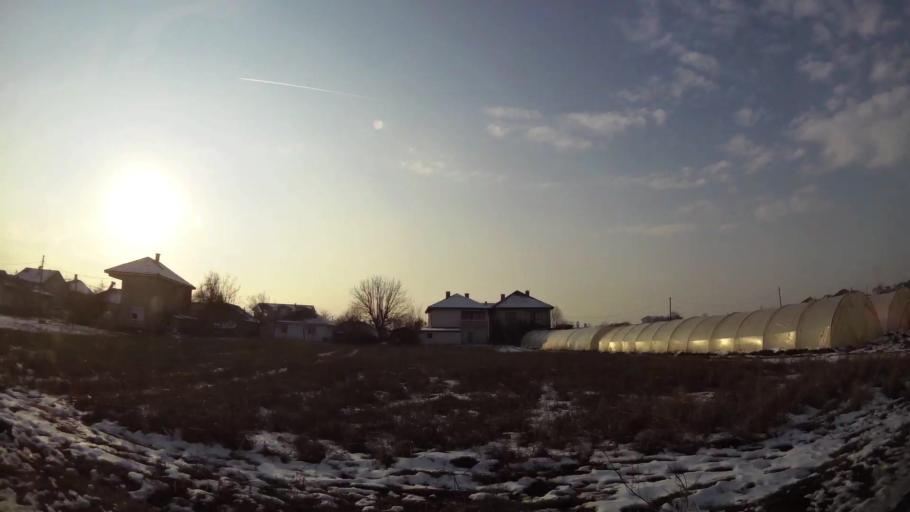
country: MK
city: Creshevo
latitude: 42.0248
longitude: 21.5197
